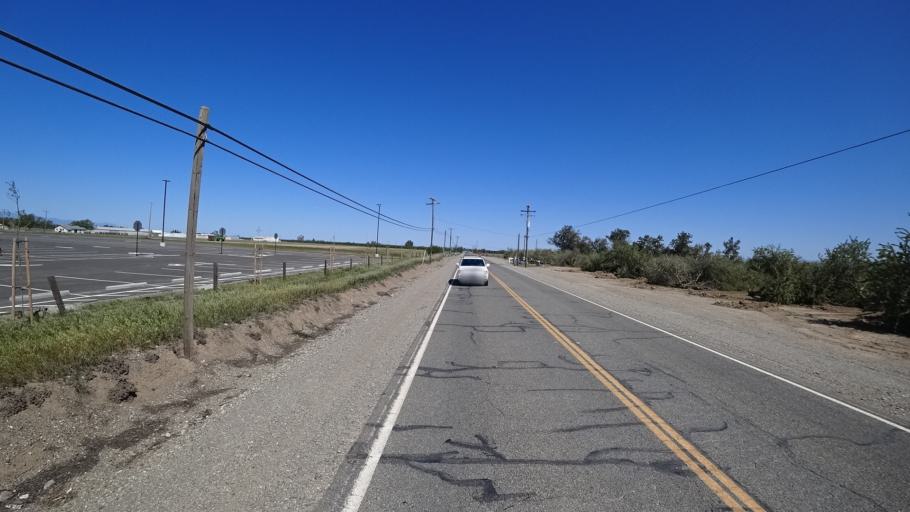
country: US
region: California
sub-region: Glenn County
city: Orland
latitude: 39.7197
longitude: -122.1410
